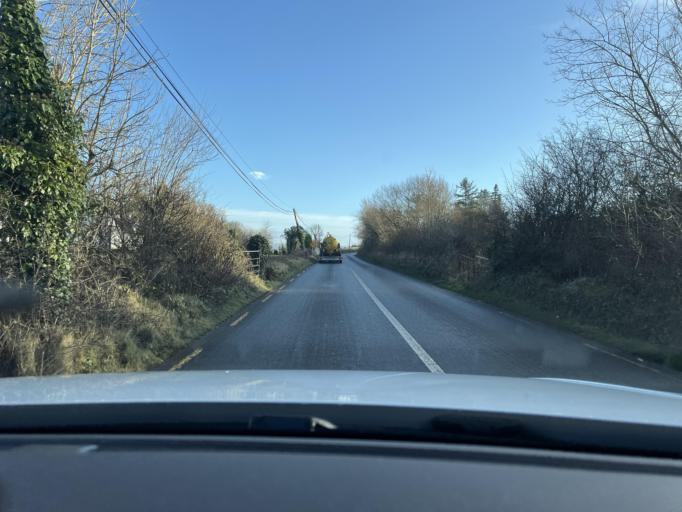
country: IE
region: Connaught
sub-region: County Leitrim
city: Manorhamilton
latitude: 54.1842
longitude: -8.1601
